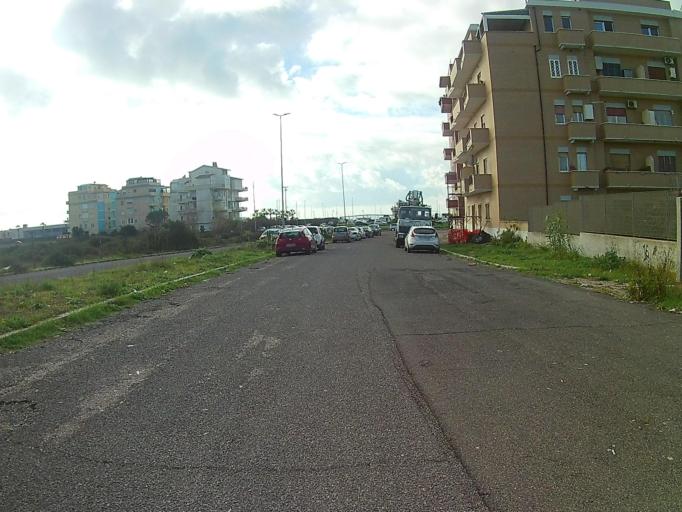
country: IT
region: Latium
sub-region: Citta metropolitana di Roma Capitale
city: Lido di Ostia
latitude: 41.7246
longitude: 12.2976
